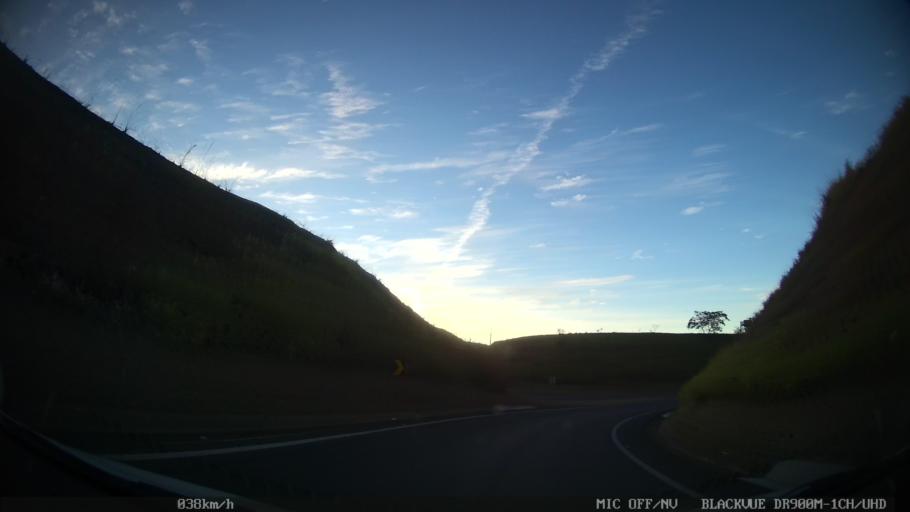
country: BR
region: Sao Paulo
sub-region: Pindorama
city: Pindorama
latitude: -21.2092
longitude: -48.9329
